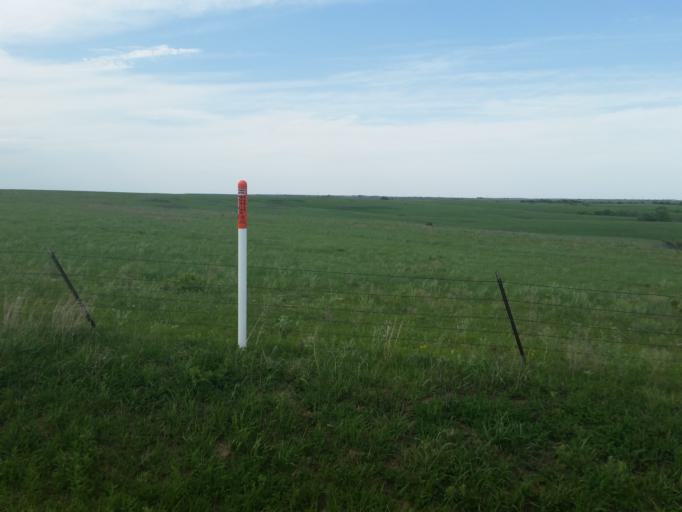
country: US
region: Kansas
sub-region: Riley County
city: Ogden
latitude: 38.9718
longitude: -96.5716
